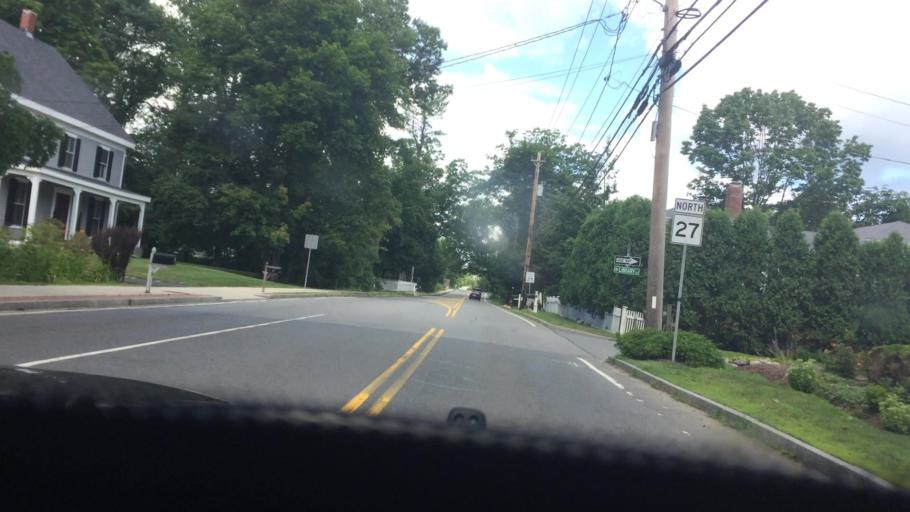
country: US
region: Massachusetts
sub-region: Middlesex County
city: Wayland
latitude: 42.3646
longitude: -71.3617
